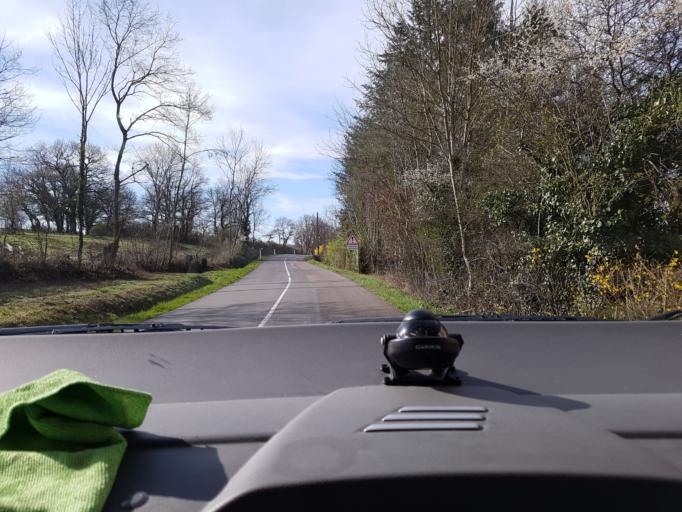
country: FR
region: Bourgogne
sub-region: Departement de Saone-et-Loire
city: Toulon-sur-Arroux
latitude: 46.7156
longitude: 4.1358
